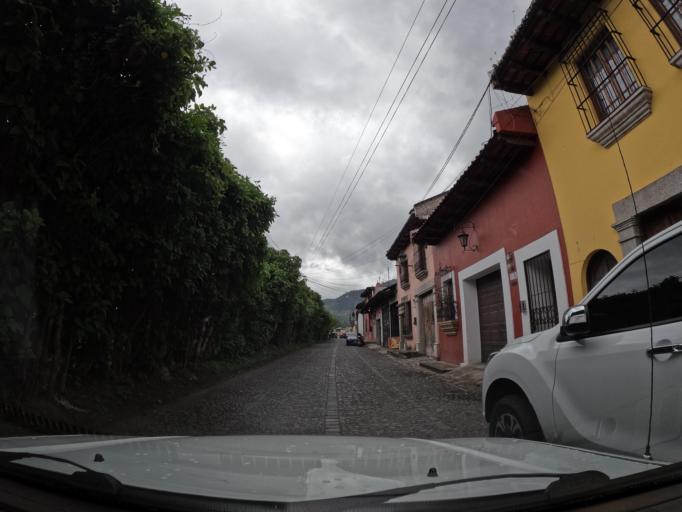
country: GT
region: Sacatepequez
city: Antigua Guatemala
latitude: 14.5647
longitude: -90.7406
